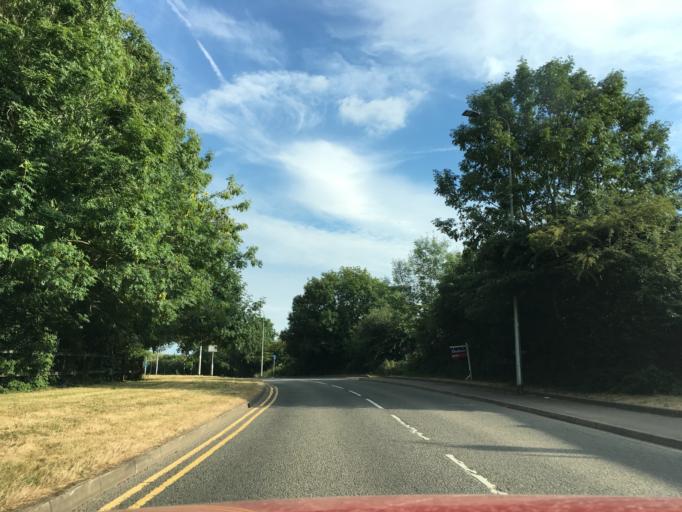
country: GB
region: Wales
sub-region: Newport
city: Marshfield
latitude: 51.5226
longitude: -3.1071
